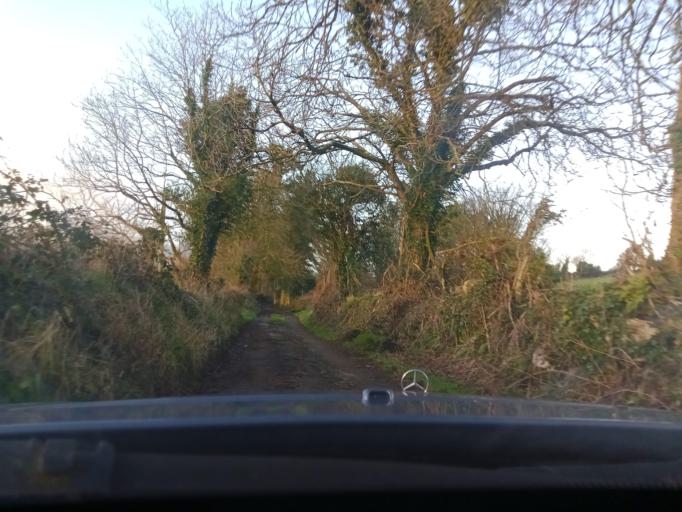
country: IE
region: Leinster
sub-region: Kilkenny
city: Callan
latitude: 52.4610
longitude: -7.4321
